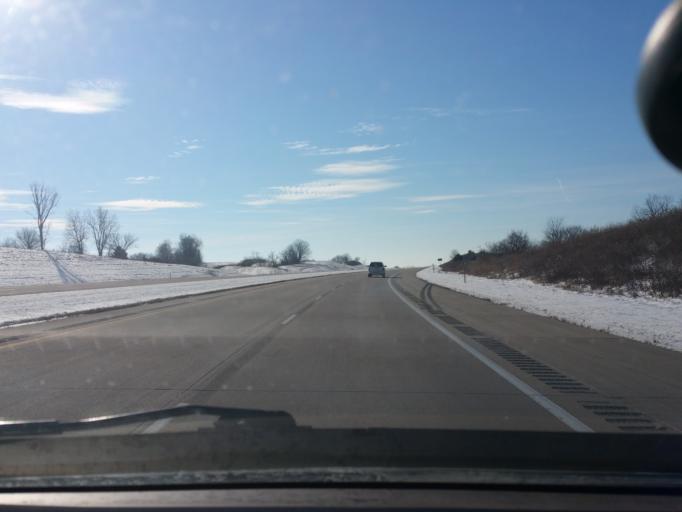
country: US
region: Iowa
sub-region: Clarke County
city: Osceola
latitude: 40.9011
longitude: -93.7970
